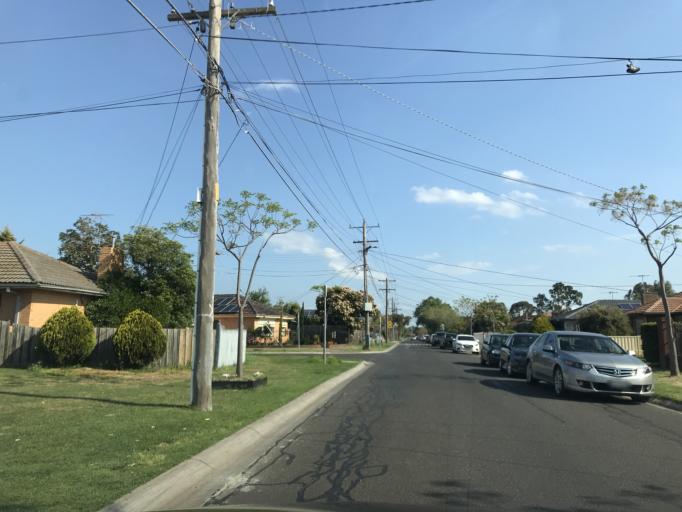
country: AU
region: Victoria
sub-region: Wyndham
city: Hoppers Crossing
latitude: -37.8796
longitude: 144.6969
